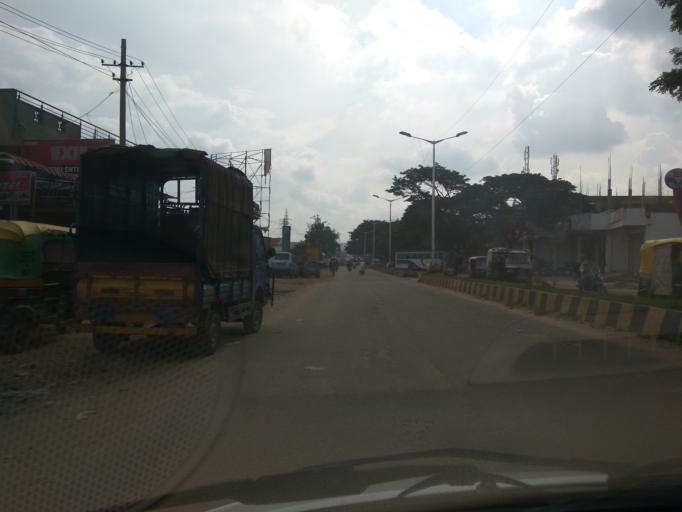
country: IN
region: Karnataka
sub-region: Kolar
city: Kolar
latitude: 13.1278
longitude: 78.1171
